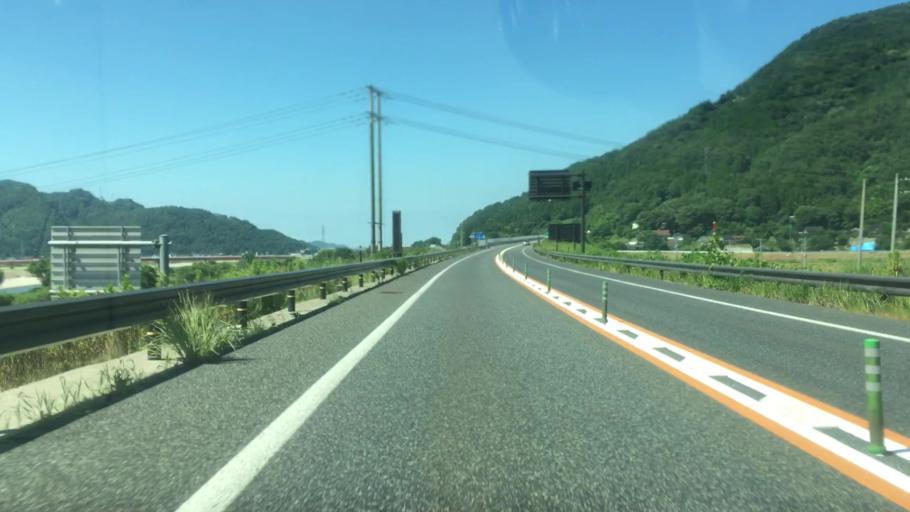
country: JP
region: Tottori
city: Tottori
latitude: 35.4022
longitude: 134.2051
